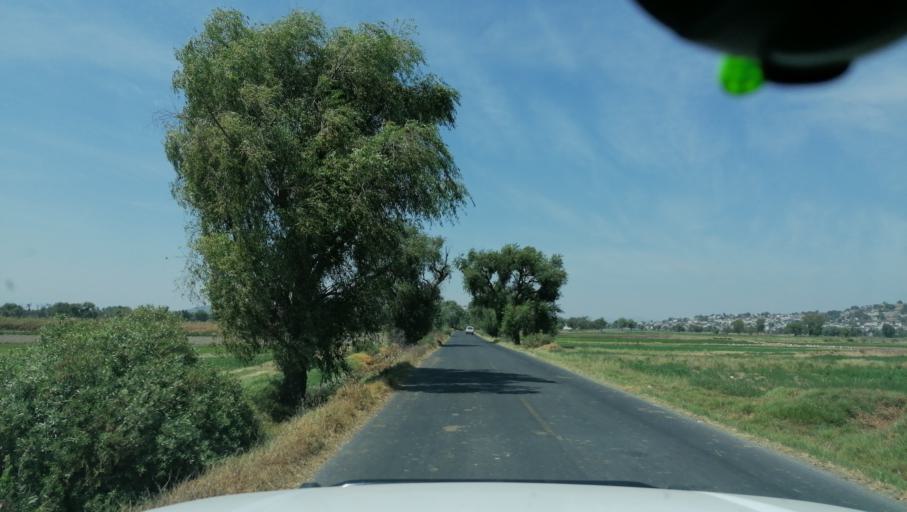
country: MX
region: Tlaxcala
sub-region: Tetlatlahuca
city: Tetlatlahuca
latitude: 19.2167
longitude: -98.2887
